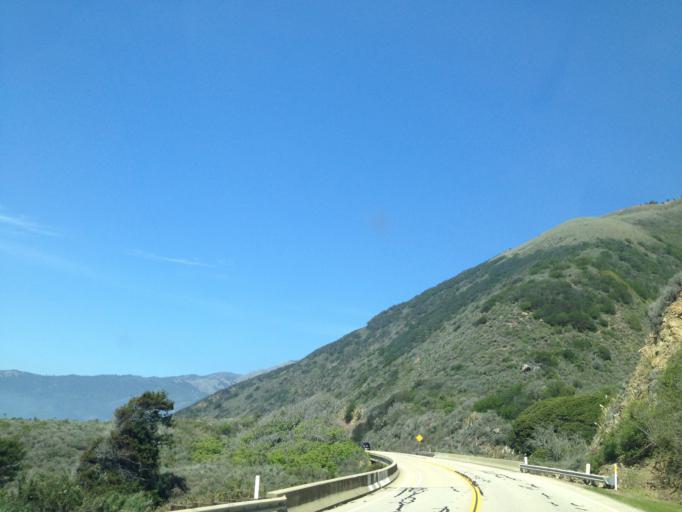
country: US
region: California
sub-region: Monterey County
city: Greenfield
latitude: 35.9676
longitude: -121.4834
